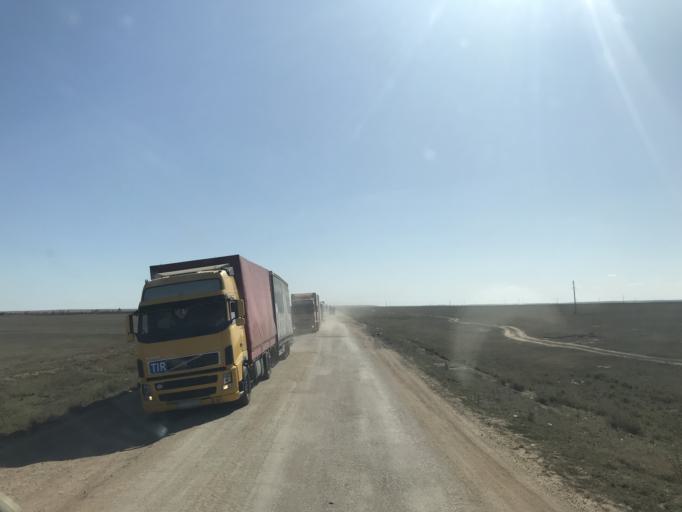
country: RU
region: Orenburg
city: Dombarovskiy
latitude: 49.9419
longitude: 60.1259
